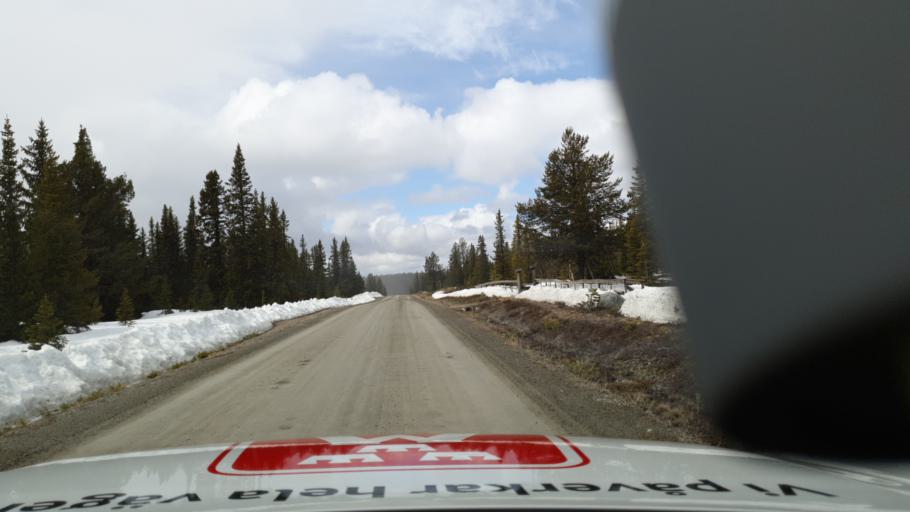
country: SE
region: Jaemtland
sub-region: Bergs Kommun
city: Hoverberg
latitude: 62.8550
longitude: 13.9128
